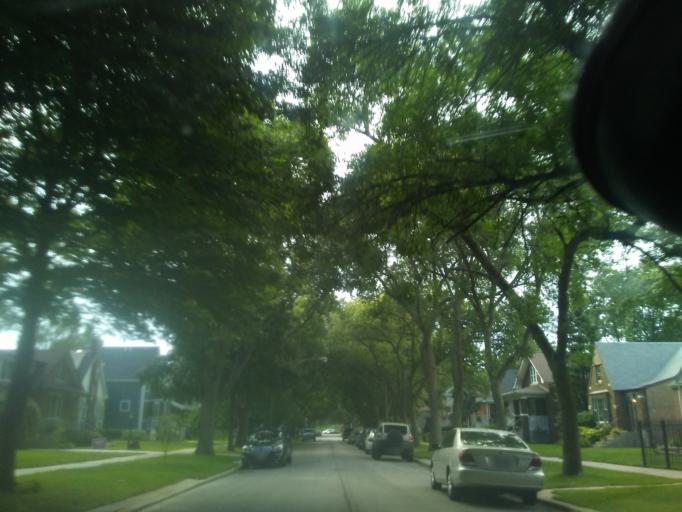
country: US
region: Illinois
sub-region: Cook County
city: Lincolnwood
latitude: 41.9779
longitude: -87.7523
